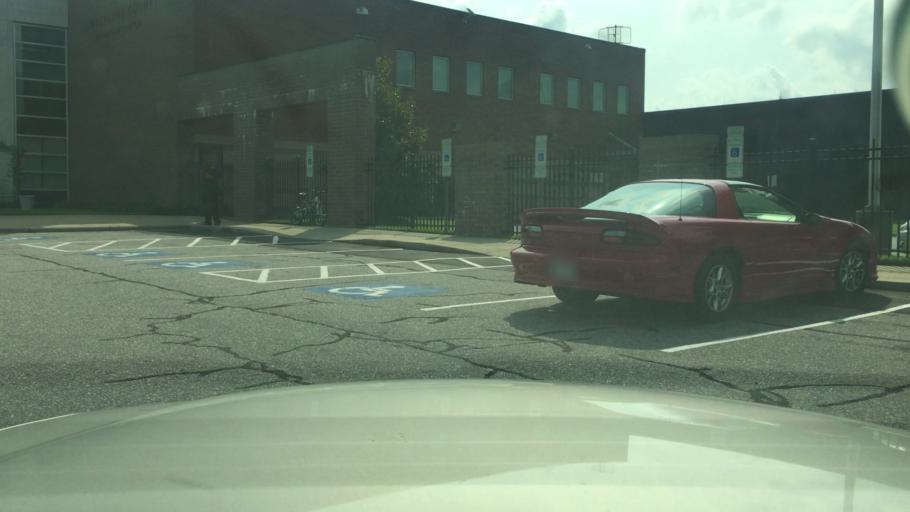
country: US
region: North Carolina
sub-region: Cumberland County
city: Fayetteville
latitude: 35.0504
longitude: -78.8797
